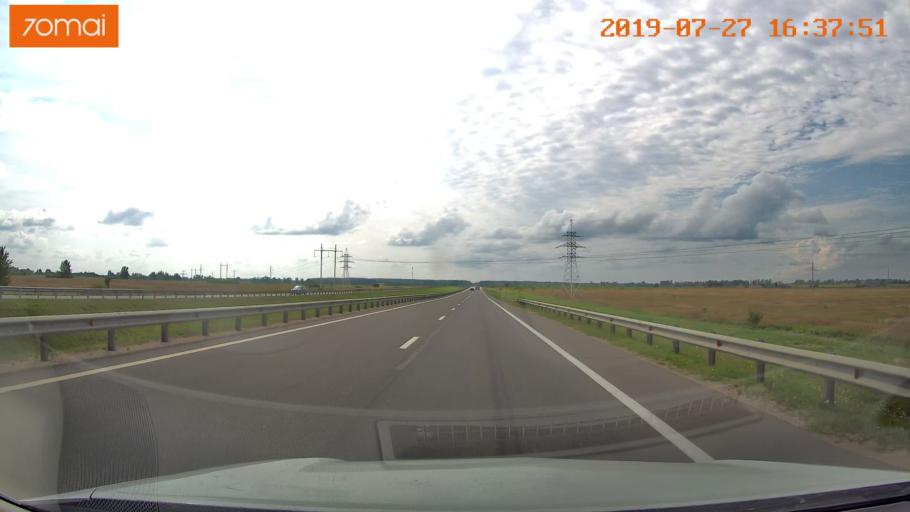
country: RU
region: Kaliningrad
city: Gvardeysk
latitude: 54.6486
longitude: 21.2447
